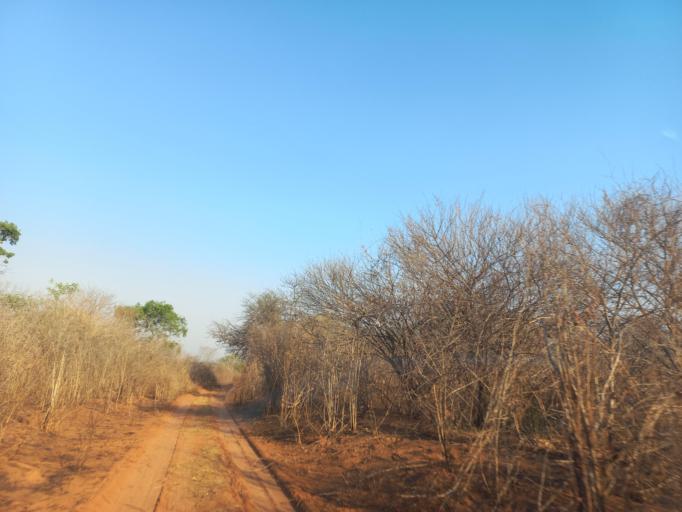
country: ZM
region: Lusaka
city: Luangwa
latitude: -15.4190
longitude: 30.2593
